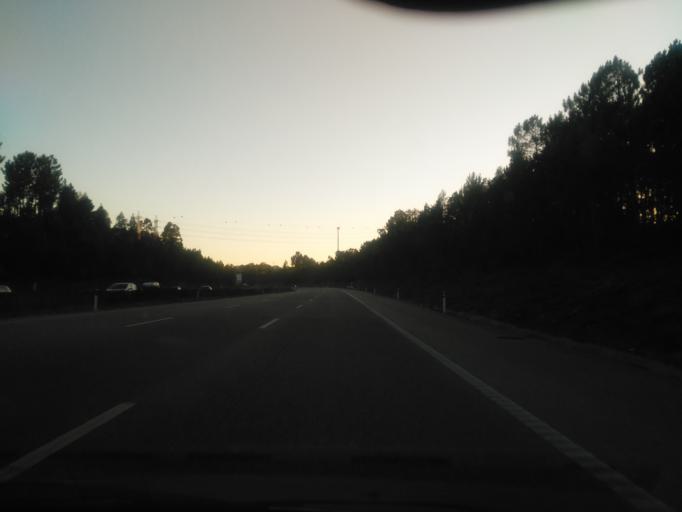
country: PT
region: Leiria
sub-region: Leiria
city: Maceira
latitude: 39.7220
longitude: -8.9060
